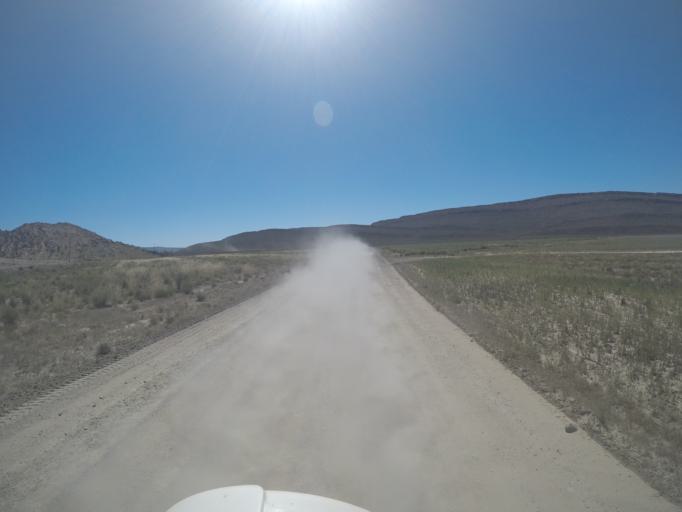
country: ZA
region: Western Cape
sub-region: Cape Winelands District Municipality
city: Ceres
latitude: -32.8317
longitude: 19.4514
